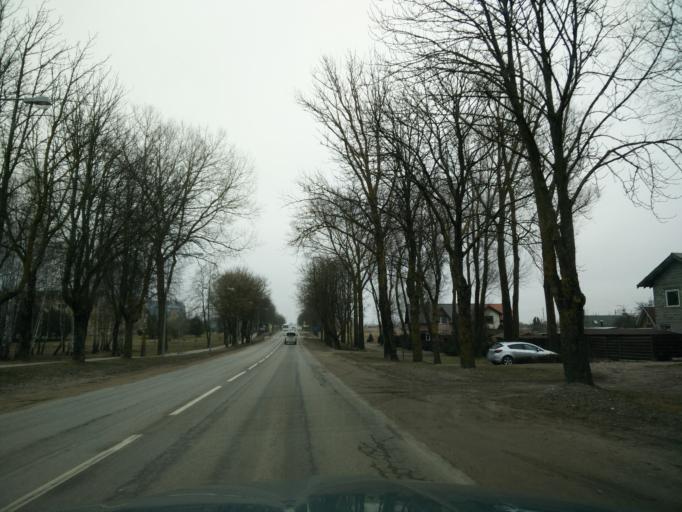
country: LT
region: Klaipedos apskritis
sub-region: Klaipeda
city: Palanga
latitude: 55.9135
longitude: 21.0842
